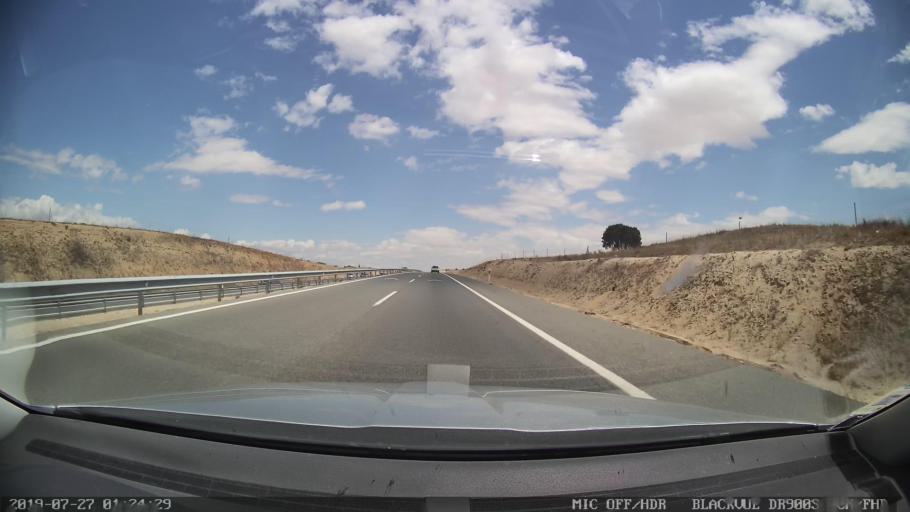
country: ES
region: Castille-La Mancha
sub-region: Province of Toledo
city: Santa Cruz del Retamar
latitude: 40.1319
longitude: -4.2076
